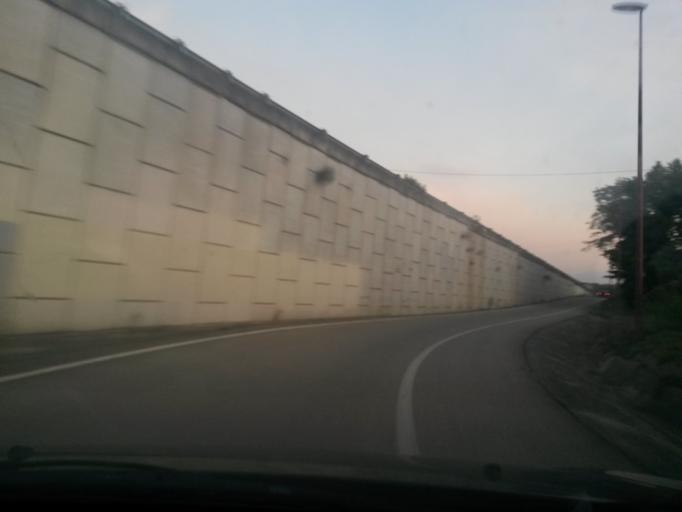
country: ES
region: Catalonia
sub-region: Provincia de Girona
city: Cornella del Terri
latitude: 42.0980
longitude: 2.7980
